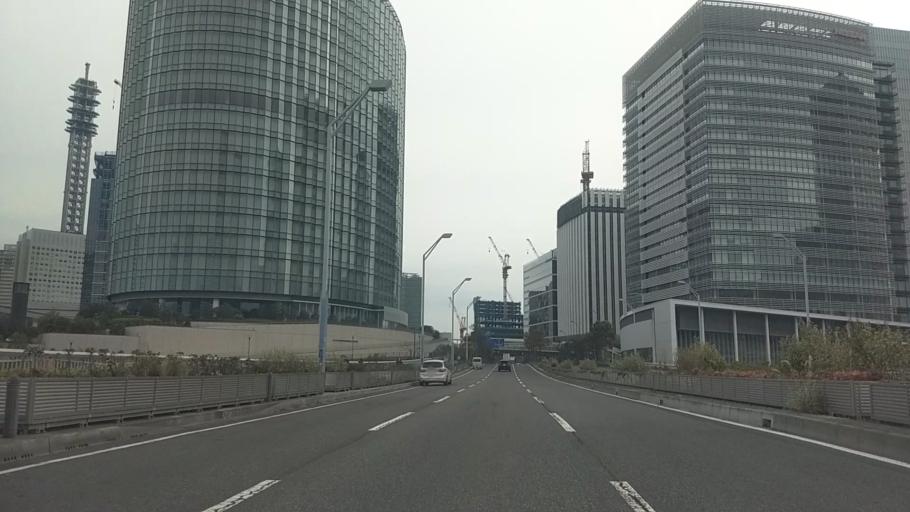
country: JP
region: Kanagawa
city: Yokohama
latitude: 35.4654
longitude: 139.6276
